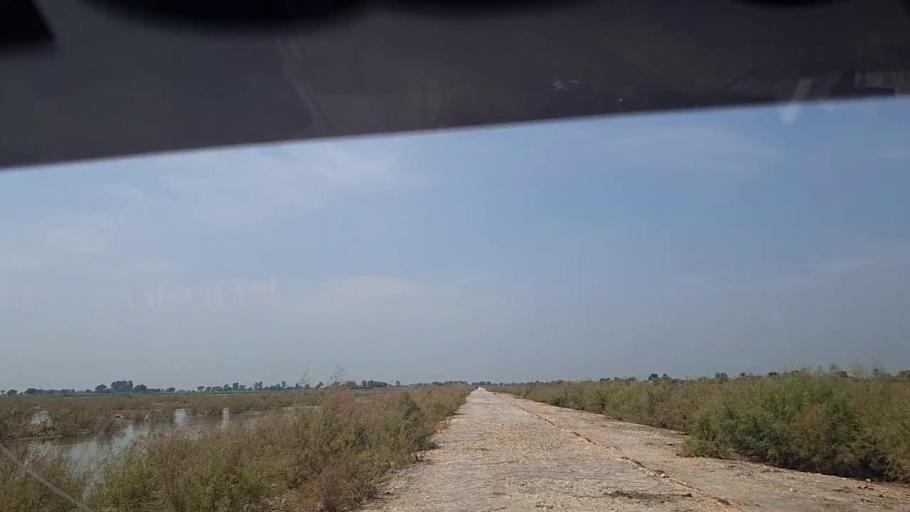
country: PK
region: Sindh
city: Thul
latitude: 28.1692
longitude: 68.7594
